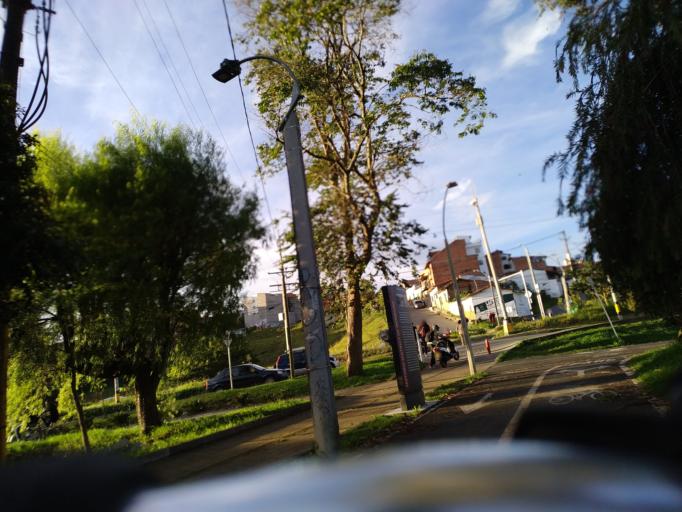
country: CO
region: Antioquia
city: Rionegro
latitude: 6.1485
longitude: -75.3757
